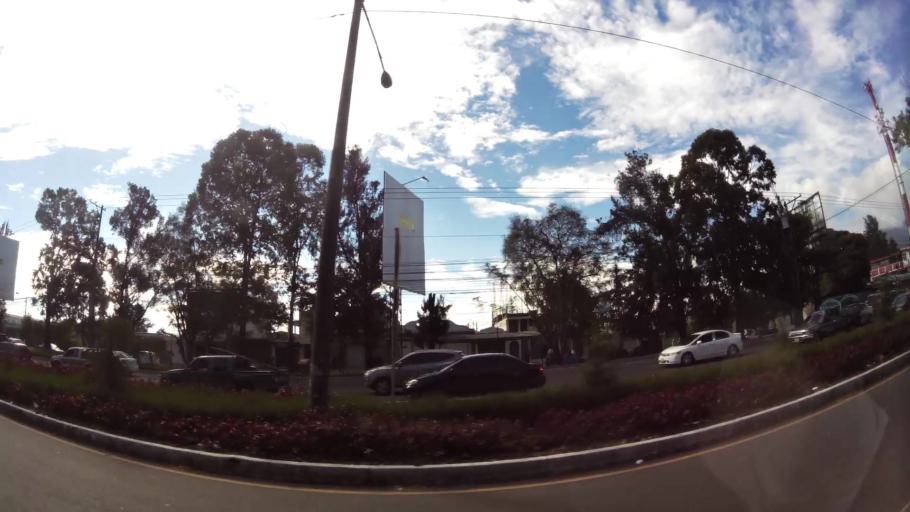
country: GT
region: Guatemala
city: Mixco
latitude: 14.6349
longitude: -90.5945
